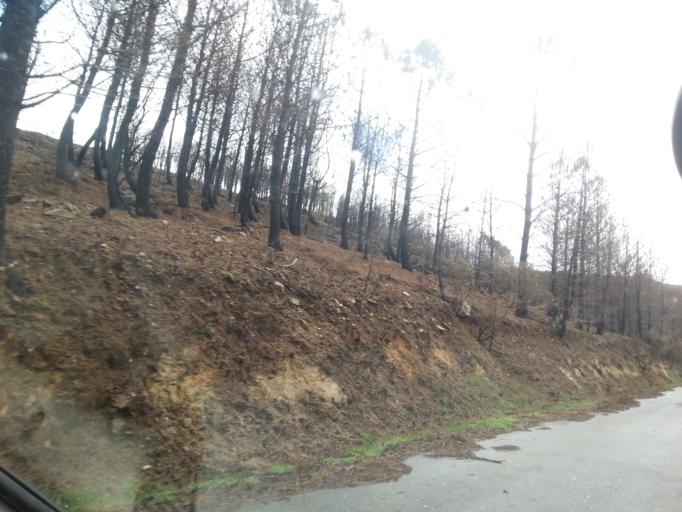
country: PT
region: Guarda
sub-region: Celorico da Beira
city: Celorico da Beira
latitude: 40.5404
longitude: -7.4484
